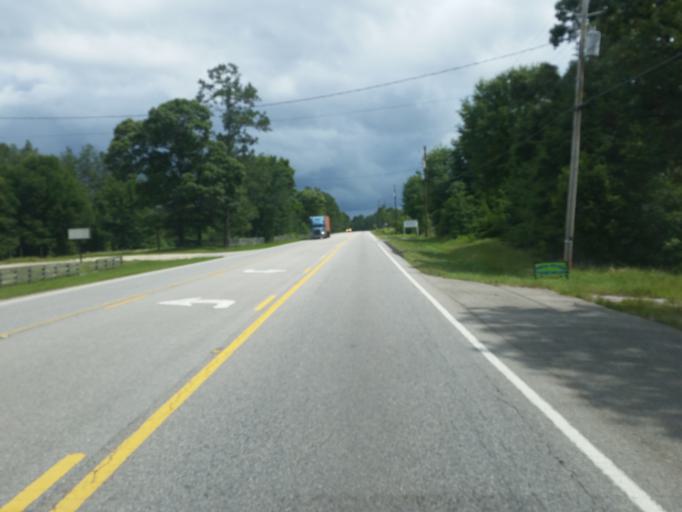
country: US
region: Mississippi
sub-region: Jackson County
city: Hurley
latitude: 30.8445
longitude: -88.3955
